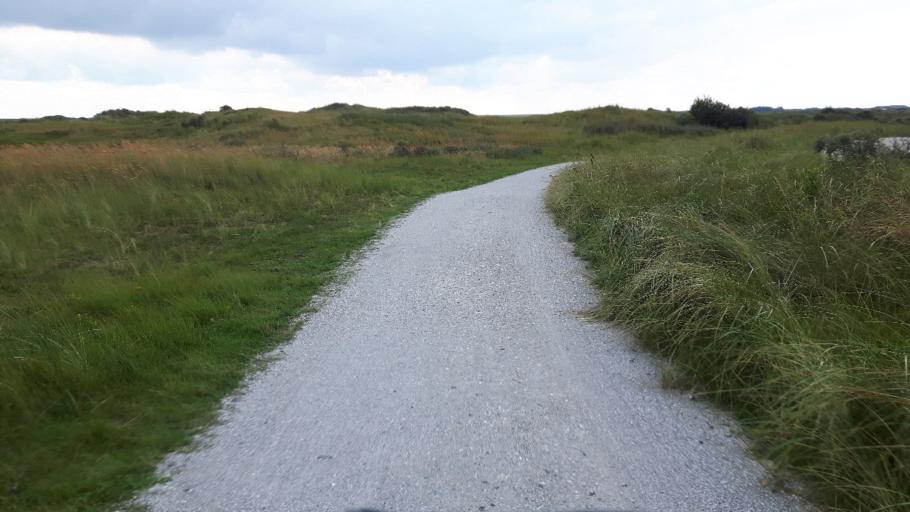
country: NL
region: Friesland
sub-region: Gemeente Ameland
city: Nes
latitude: 53.4573
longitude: 5.8292
